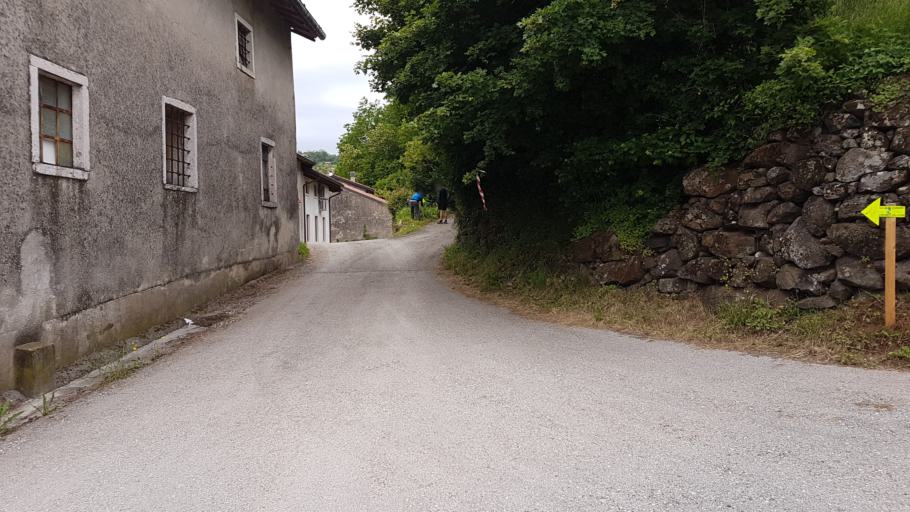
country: IT
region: Veneto
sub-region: Provincia di Vicenza
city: Nogarole Vicentino
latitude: 45.5533
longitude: 11.3201
